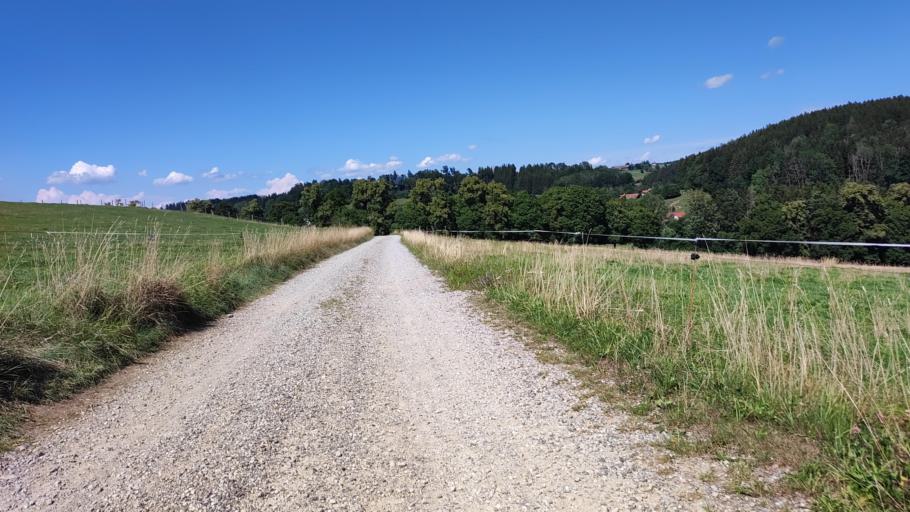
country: DE
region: Bavaria
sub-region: Swabia
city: Obergunzburg
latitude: 47.8459
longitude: 10.4267
